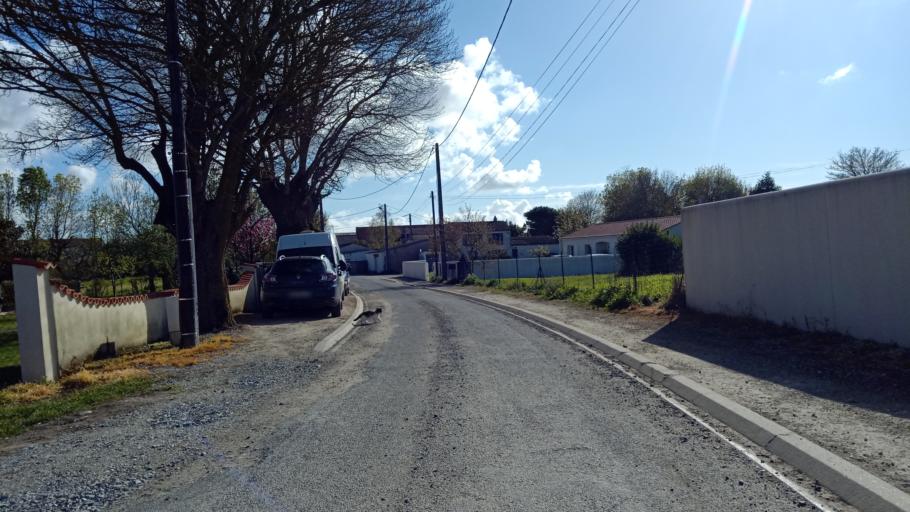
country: FR
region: Poitou-Charentes
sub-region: Departement de la Charente-Maritime
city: Verines
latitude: 46.1673
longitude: -0.9470
